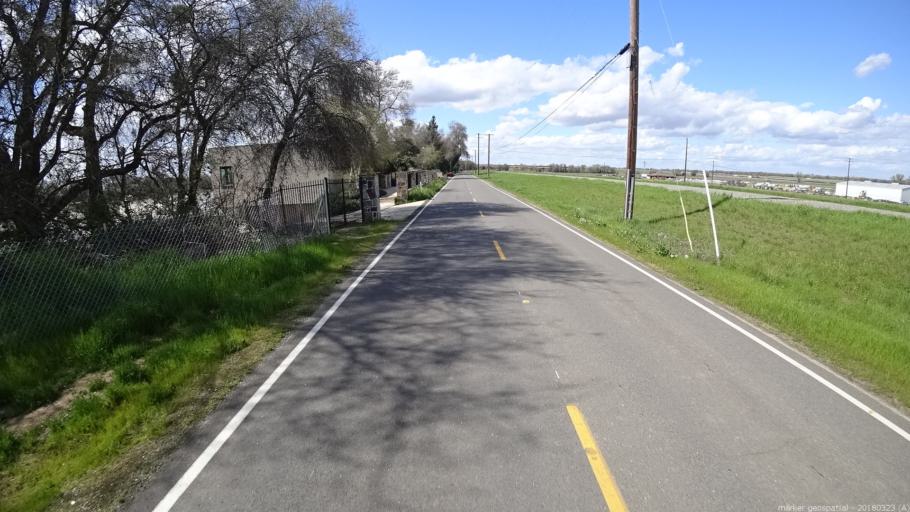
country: US
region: California
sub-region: Yolo County
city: West Sacramento
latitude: 38.6665
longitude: -121.6146
